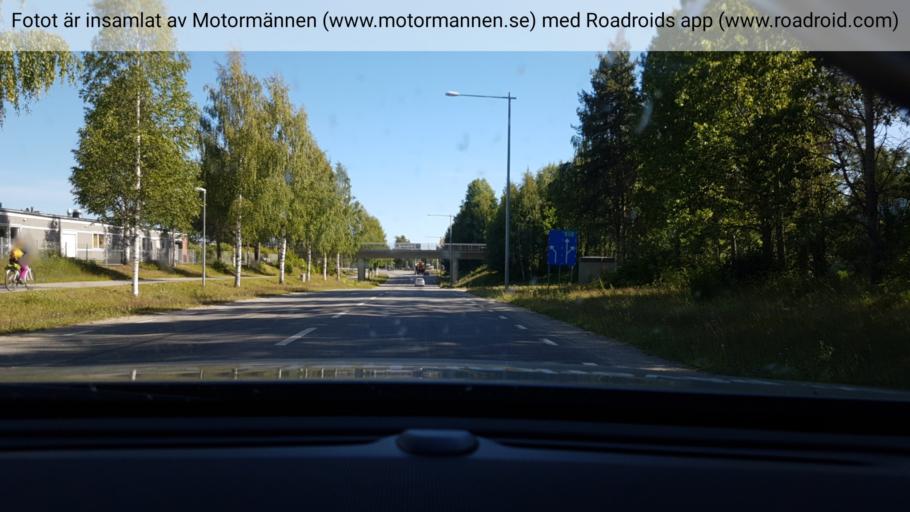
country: SE
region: Vaesterbotten
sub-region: Lycksele Kommun
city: Lycksele
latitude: 64.5880
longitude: 18.6928
